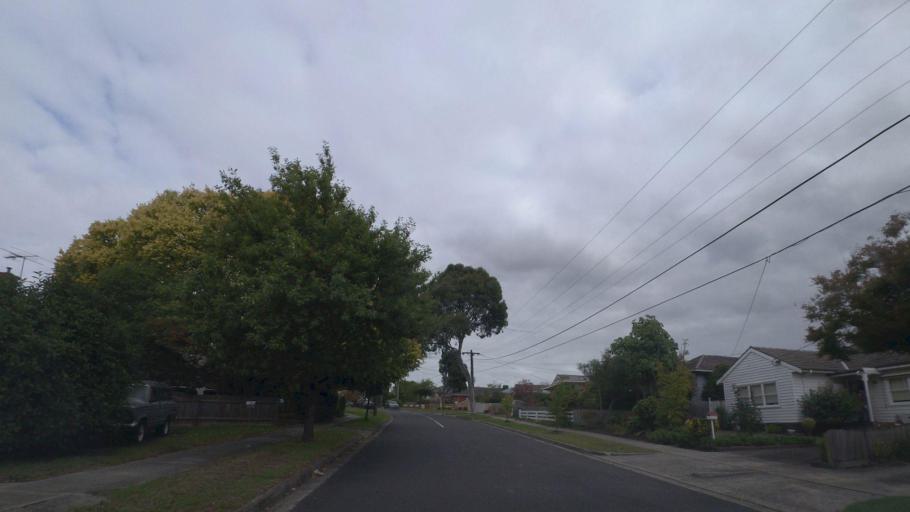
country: AU
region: Victoria
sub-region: Whitehorse
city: Nunawading
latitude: -37.8140
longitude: 145.1803
